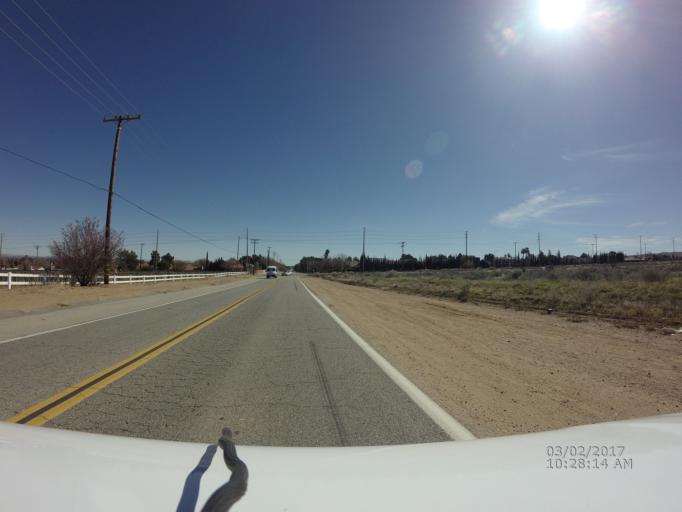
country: US
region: California
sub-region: Los Angeles County
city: Quartz Hill
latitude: 34.6382
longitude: -118.2375
